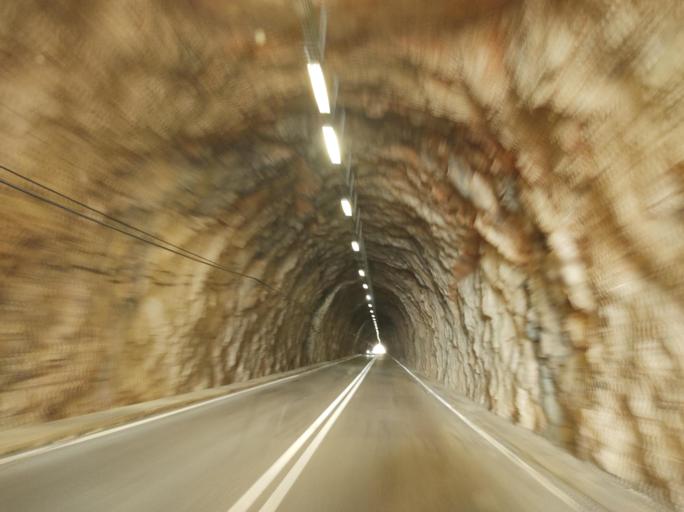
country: ES
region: Balearic Islands
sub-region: Illes Balears
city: Fornalutx
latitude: 39.7903
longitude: 2.7746
